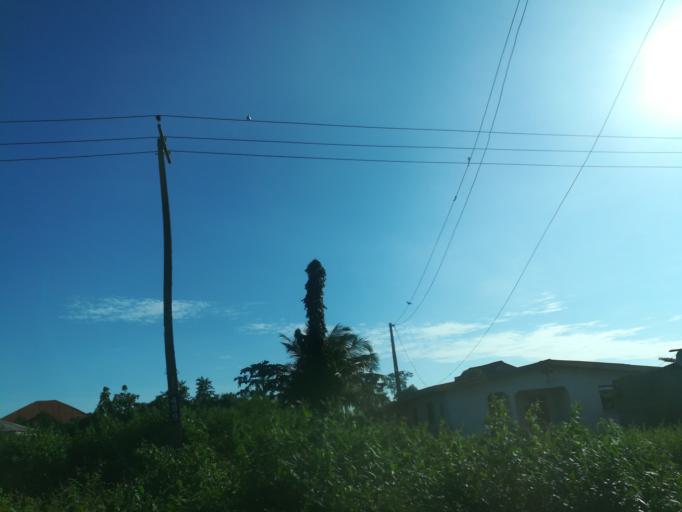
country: NG
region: Lagos
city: Ebute Ikorodu
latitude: 6.5396
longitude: 3.5499
